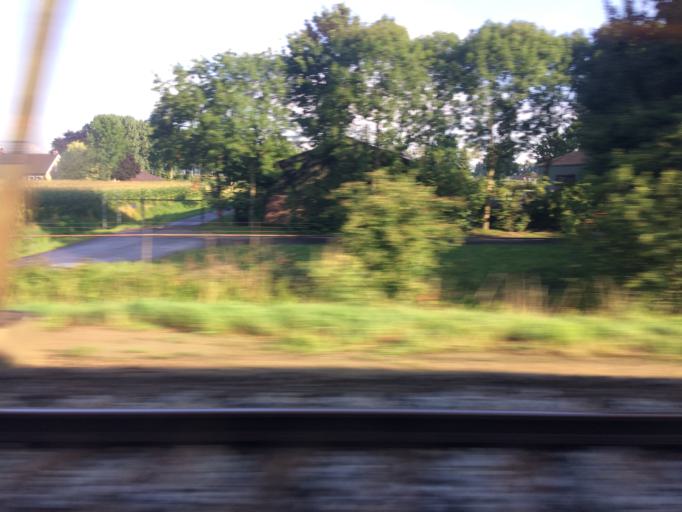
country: NL
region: North Brabant
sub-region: Gemeente Maasdonk
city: Geffen
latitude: 51.7400
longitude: 5.4519
